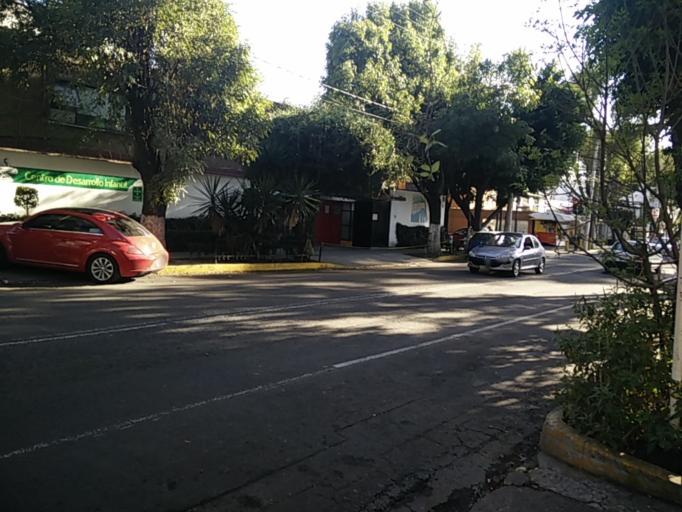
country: MX
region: Mexico
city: Colonia Lindavista
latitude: 19.4911
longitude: -99.1269
